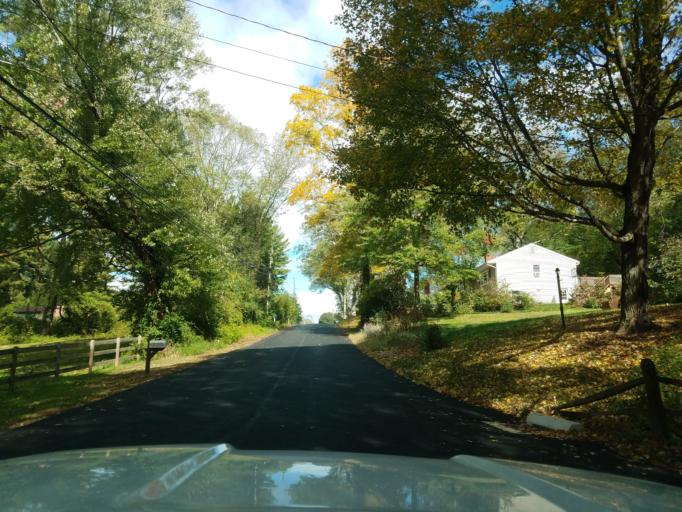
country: US
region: Connecticut
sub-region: Tolland County
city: South Coventry
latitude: 41.7181
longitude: -72.2910
